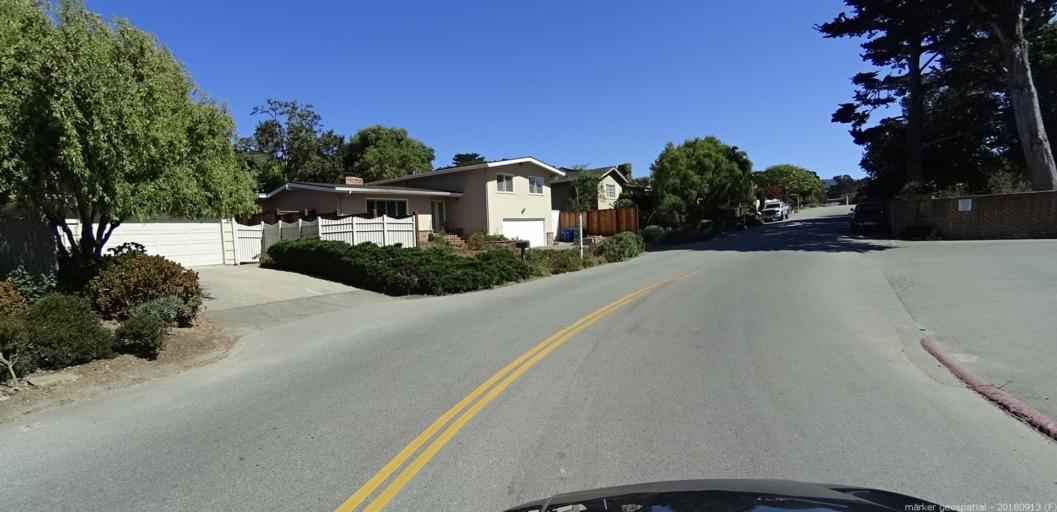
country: US
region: California
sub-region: Monterey County
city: Carmel-by-the-Sea
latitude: 36.5429
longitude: -121.9209
